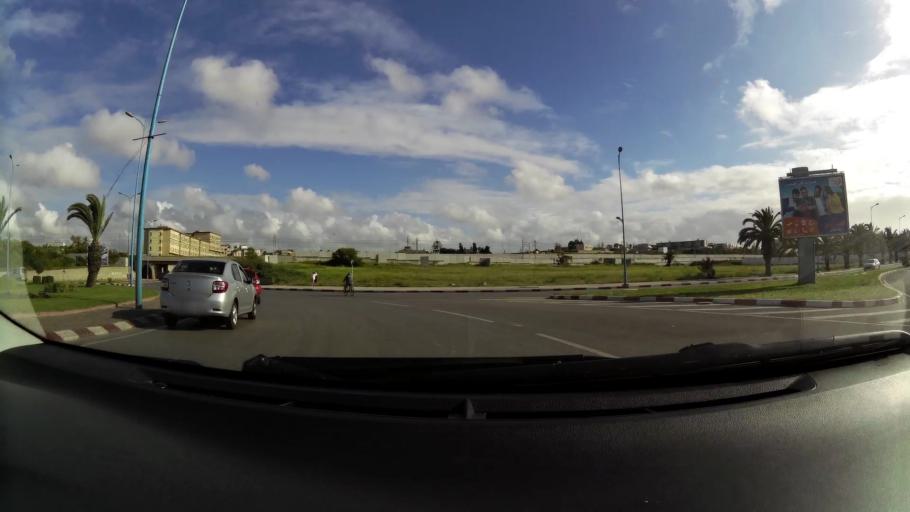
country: MA
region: Grand Casablanca
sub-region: Mohammedia
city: Mohammedia
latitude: 33.7035
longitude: -7.3725
